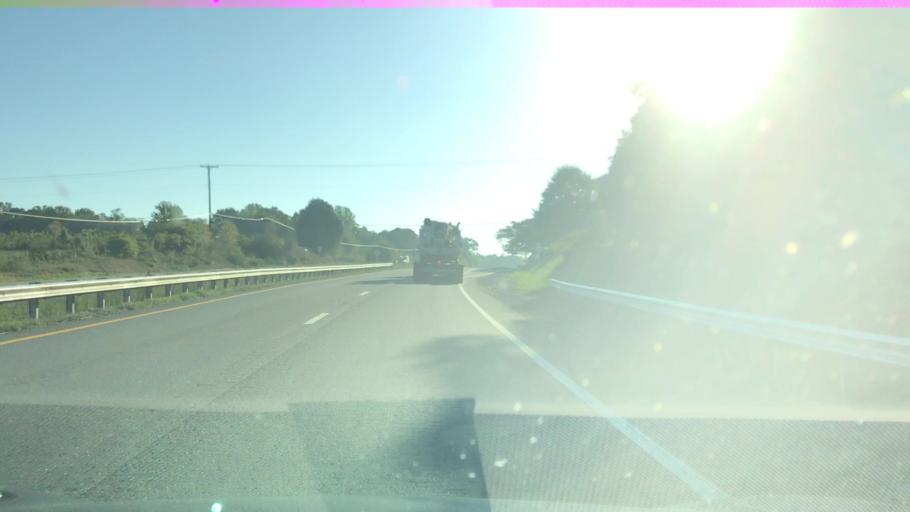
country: US
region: Virginia
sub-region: City of Bedford
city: Bedford
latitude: 37.3192
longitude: -79.4342
